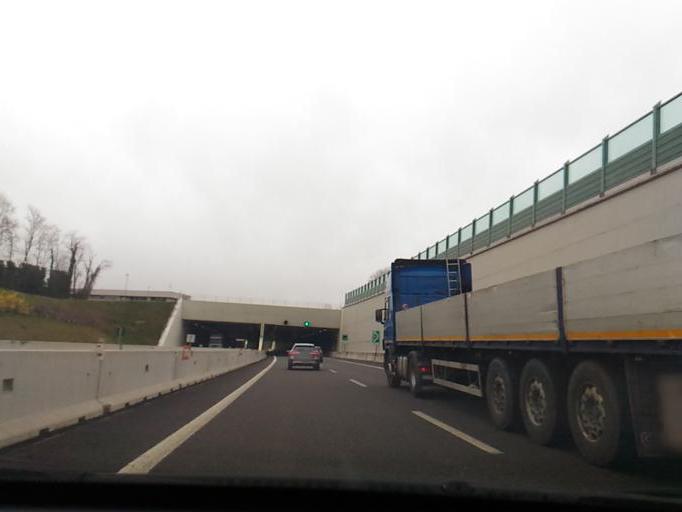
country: IT
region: Lombardy
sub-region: Provincia di Varese
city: Solbiate Olona
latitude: 45.6541
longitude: 8.8668
